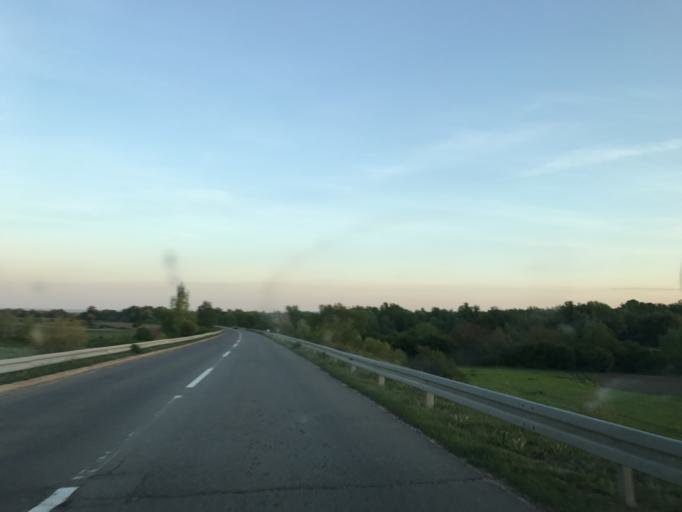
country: RS
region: Central Serbia
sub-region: Borski Okrug
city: Negotin
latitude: 44.2763
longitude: 22.5080
